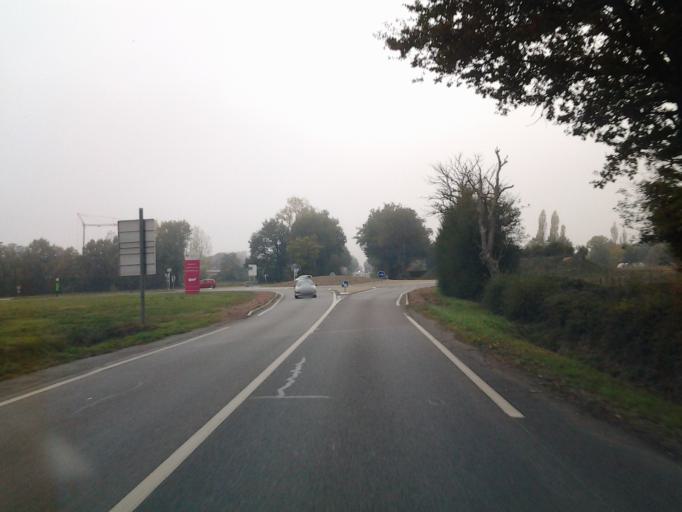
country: FR
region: Pays de la Loire
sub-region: Departement de la Vendee
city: Nesmy
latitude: 46.6218
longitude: -1.3669
